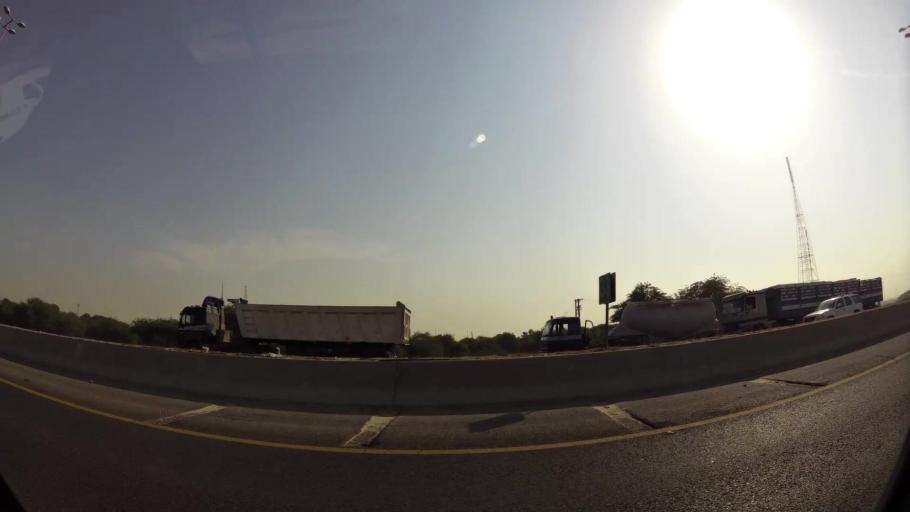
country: KW
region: Al Ahmadi
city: Al Ahmadi
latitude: 29.0834
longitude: 48.0994
